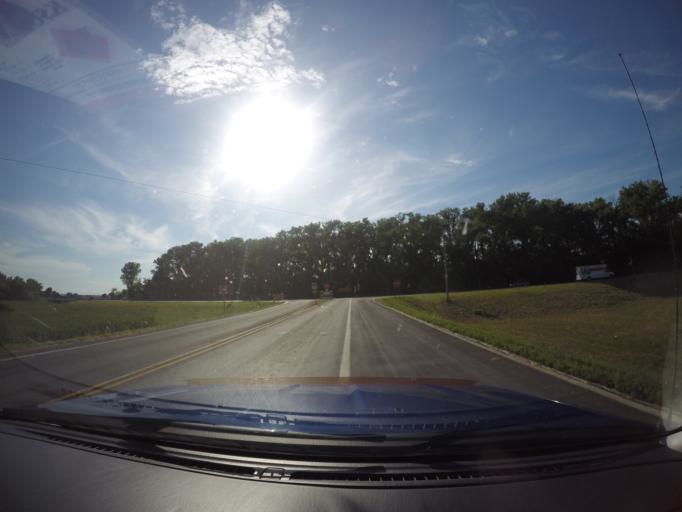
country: US
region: Kansas
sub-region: Douglas County
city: Lawrence
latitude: 39.0029
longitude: -95.1888
